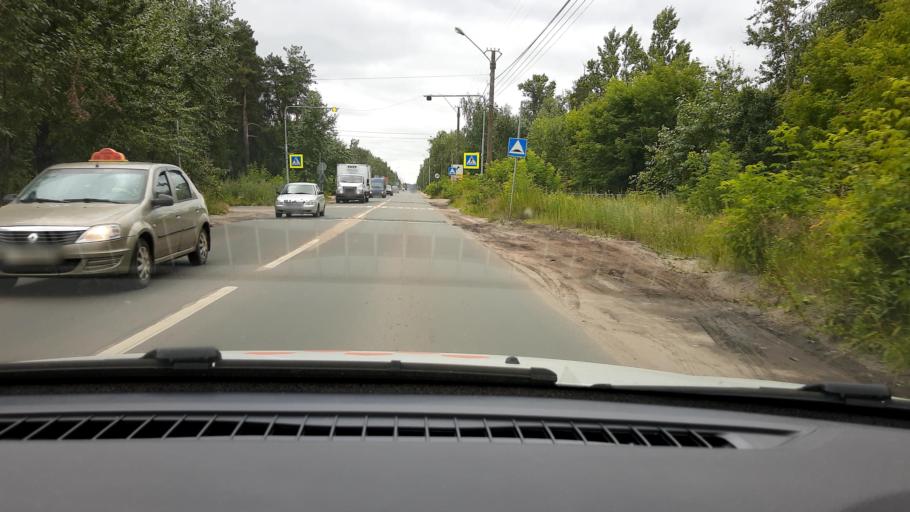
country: RU
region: Nizjnij Novgorod
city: Pyra
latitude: 56.2459
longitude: 43.3906
